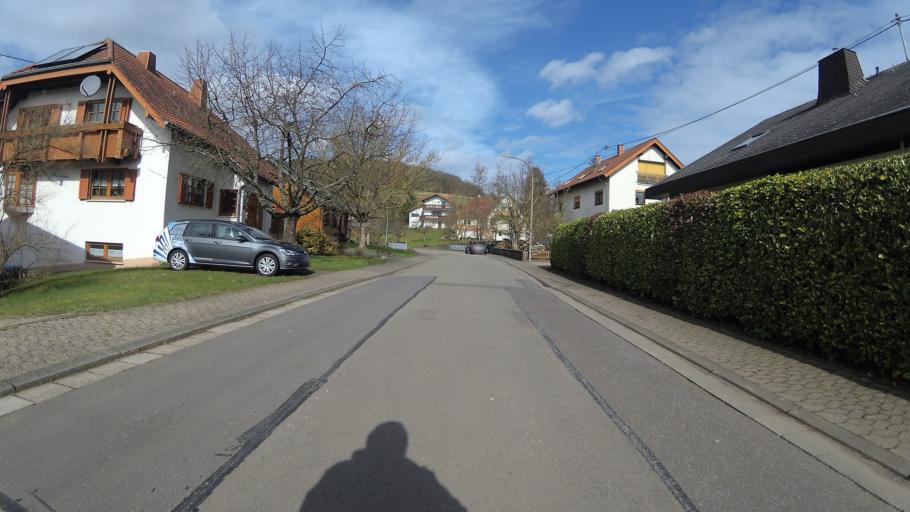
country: DE
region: Saarland
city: Sankt Wendel
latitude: 49.4817
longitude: 7.1776
